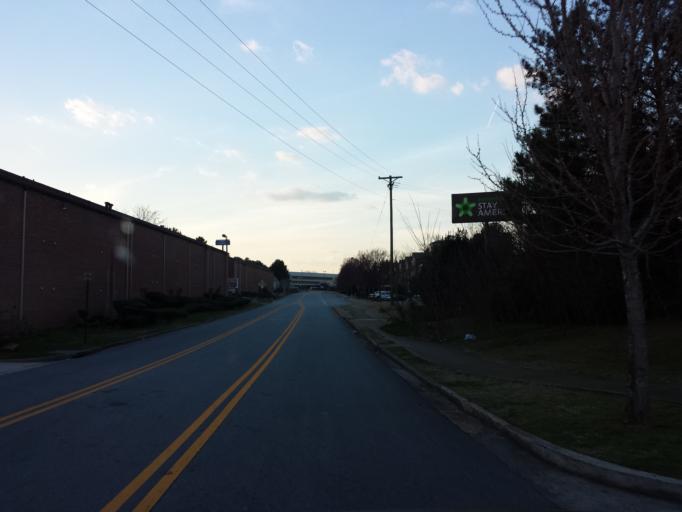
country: US
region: Georgia
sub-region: Cobb County
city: Vinings
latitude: 33.9034
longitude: -84.4726
